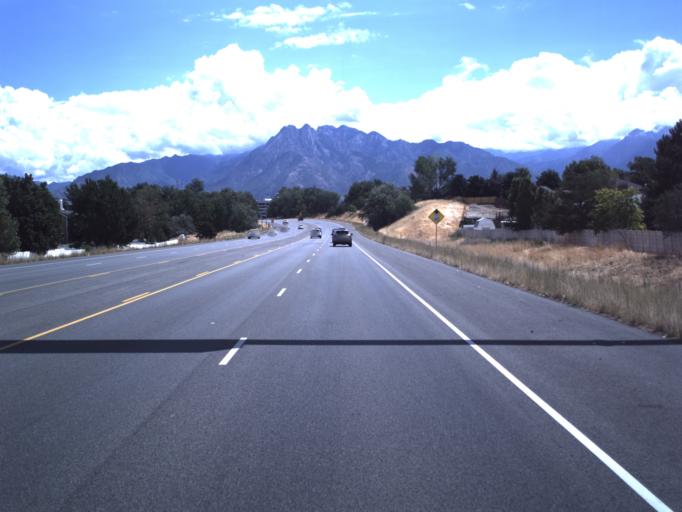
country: US
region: Utah
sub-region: Salt Lake County
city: Taylorsville
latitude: 40.6530
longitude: -111.9182
